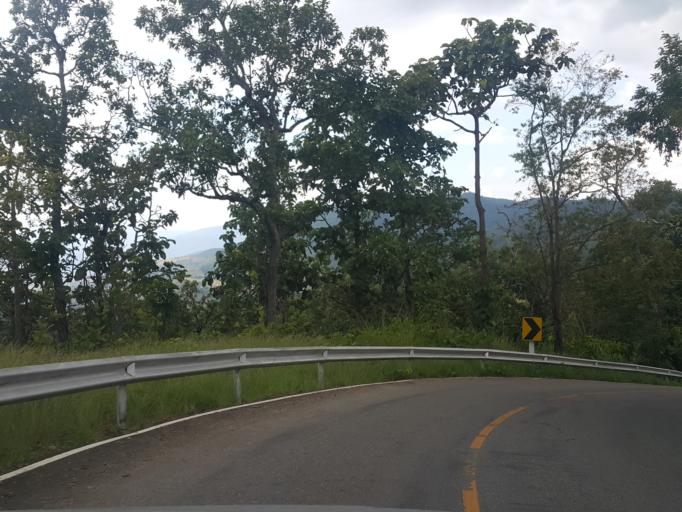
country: TH
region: Chiang Mai
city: Mae Chaem
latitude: 18.5129
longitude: 98.4255
